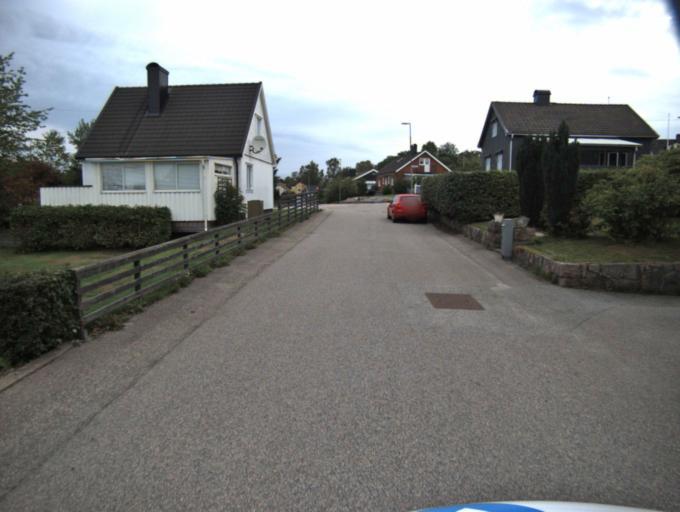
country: SE
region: Vaestra Goetaland
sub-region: Ulricehamns Kommun
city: Ulricehamn
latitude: 57.8008
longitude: 13.4293
